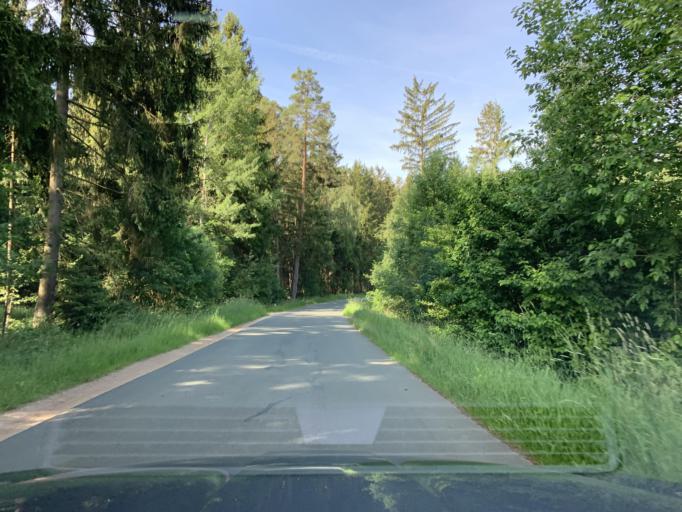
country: DE
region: Bavaria
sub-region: Upper Palatinate
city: Schwarzhofen
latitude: 49.4031
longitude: 12.3392
